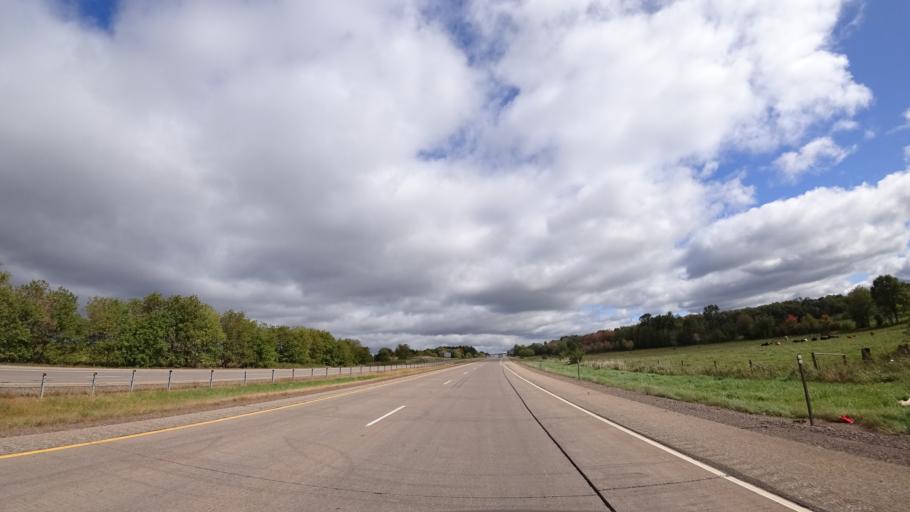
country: US
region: Wisconsin
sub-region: Chippewa County
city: Chippewa Falls
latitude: 44.9199
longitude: -91.3581
